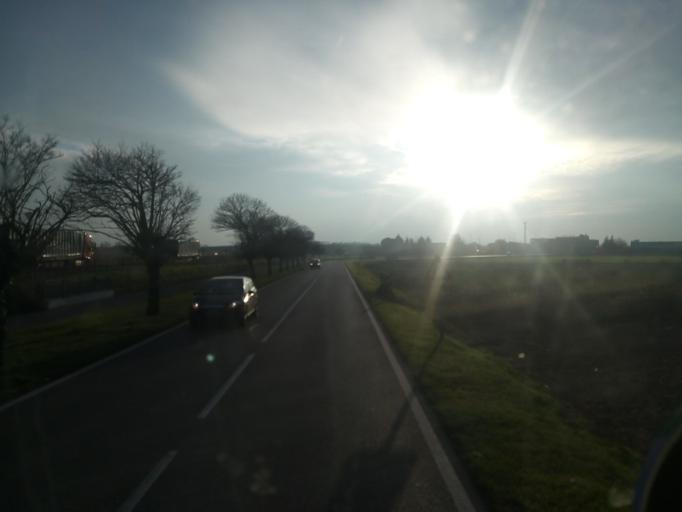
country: IT
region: Veneto
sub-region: Provincia di Verona
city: Nogarole Rocca
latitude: 45.2837
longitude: 10.8832
